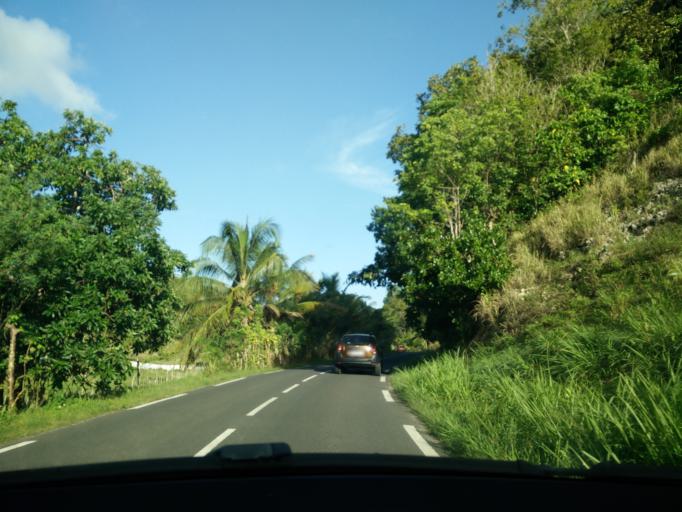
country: GP
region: Guadeloupe
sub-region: Guadeloupe
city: Sainte-Anne
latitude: 16.2770
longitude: -61.4177
